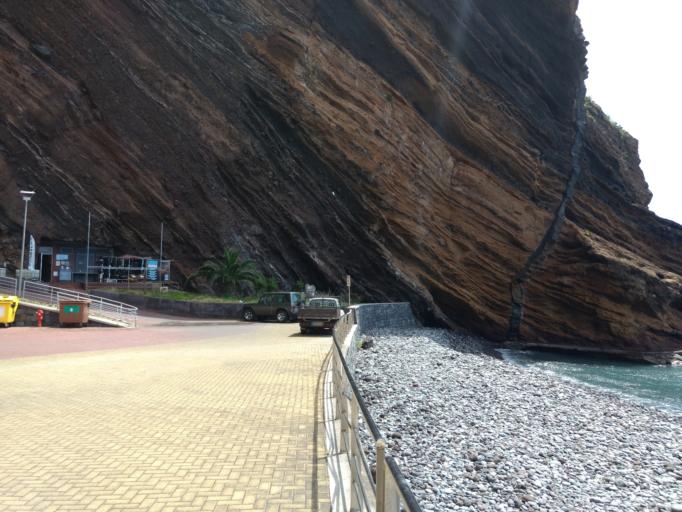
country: PT
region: Madeira
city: Canico
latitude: 32.6383
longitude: -16.8520
